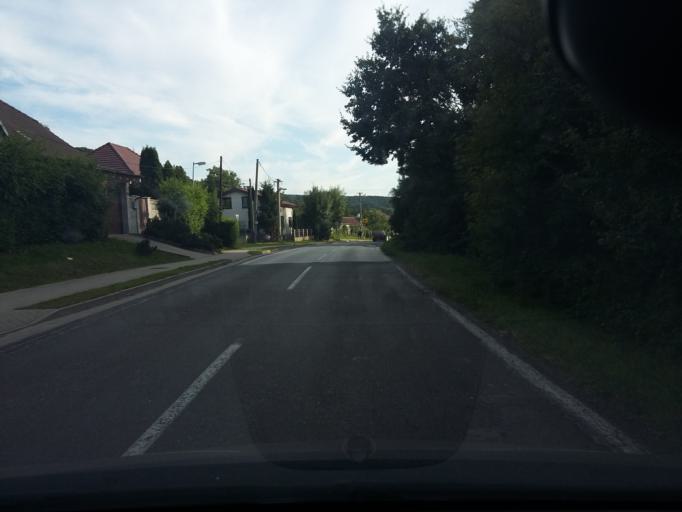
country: SK
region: Bratislavsky
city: Svaty Jur
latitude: 48.3710
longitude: 17.1471
